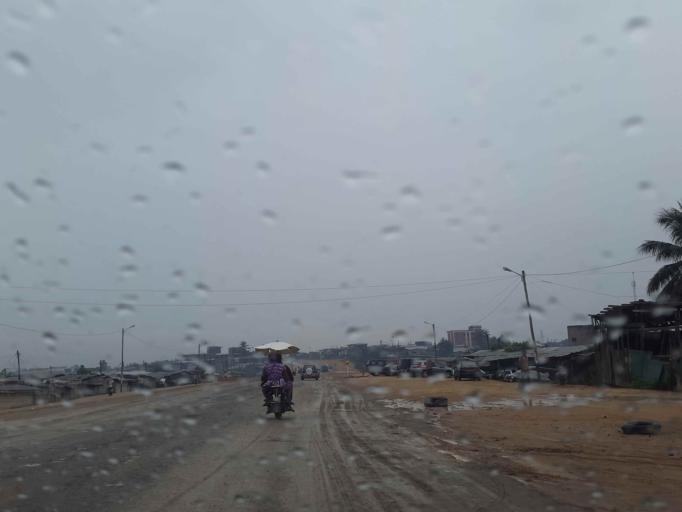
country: CM
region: Littoral
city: Douala
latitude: 4.0817
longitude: 9.7284
